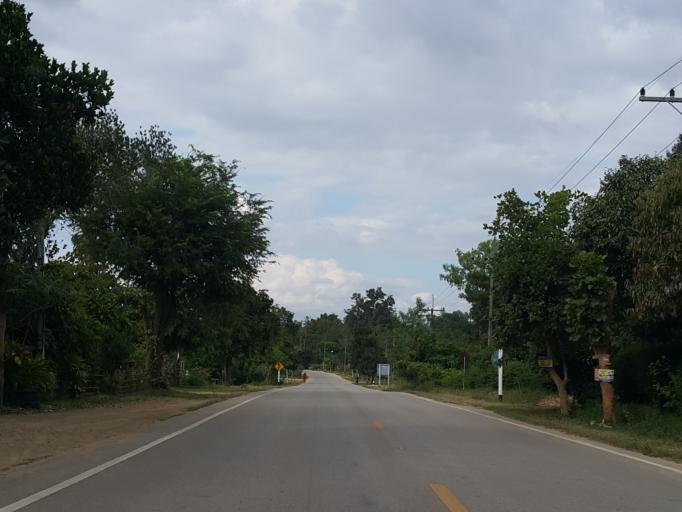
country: TH
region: Lampang
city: Chae Hom
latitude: 18.5659
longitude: 99.4727
